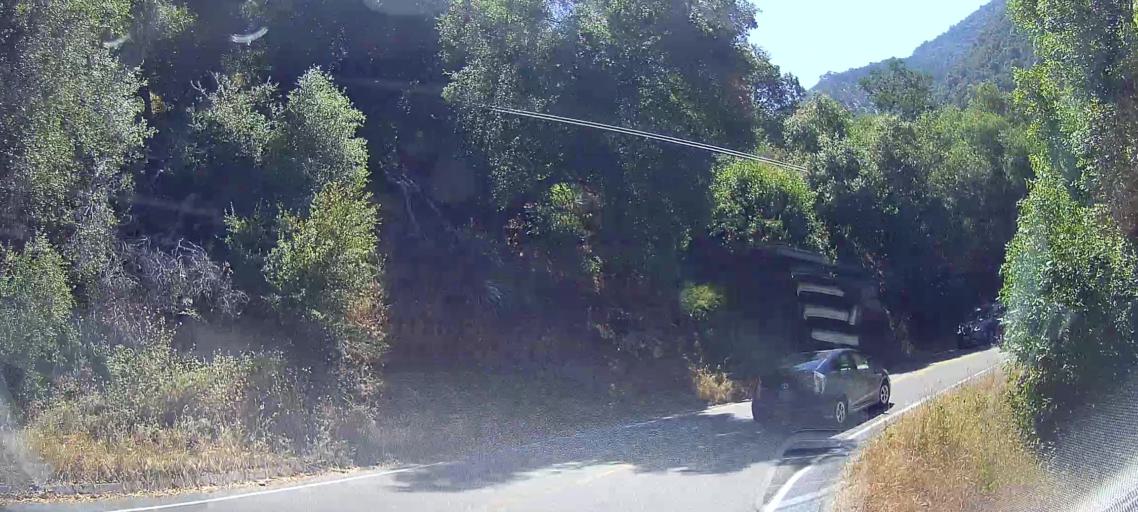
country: US
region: California
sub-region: Tulare County
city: Three Rivers
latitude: 36.5202
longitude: -118.7785
